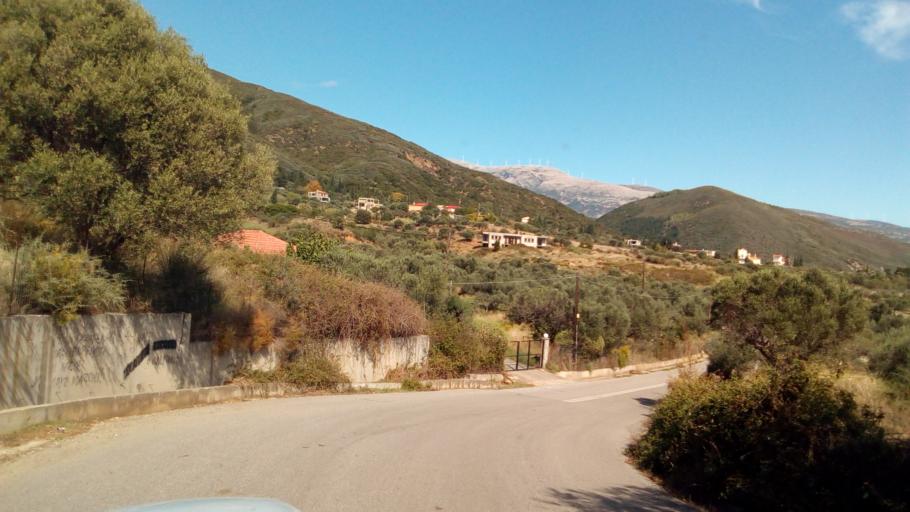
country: GR
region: West Greece
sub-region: Nomos Aitolias kai Akarnanias
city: Antirrio
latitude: 38.3640
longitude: 21.7642
